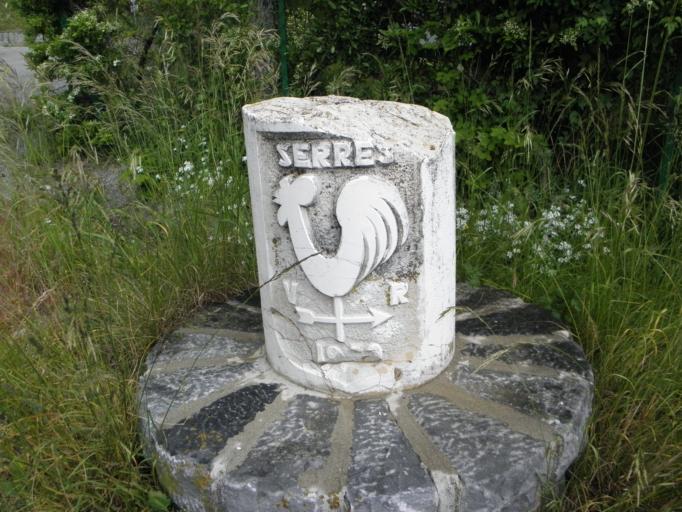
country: FR
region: Provence-Alpes-Cote d'Azur
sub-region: Departement des Hautes-Alpes
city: Serres
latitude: 44.4305
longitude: 5.7159
